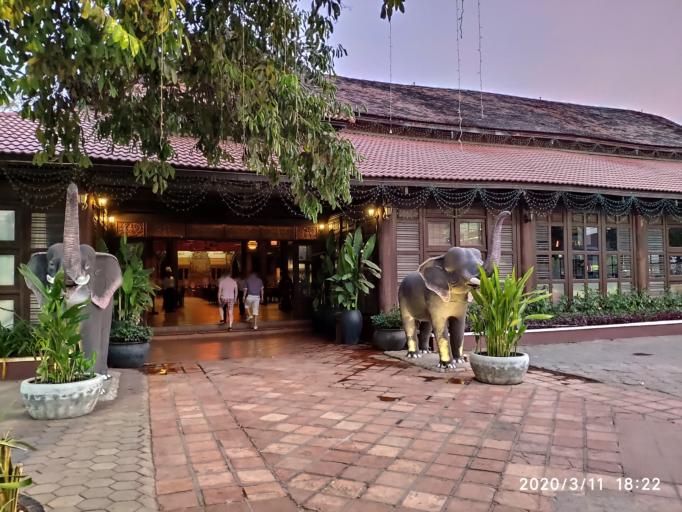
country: KH
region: Siem Reap
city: Siem Reap
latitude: 13.3622
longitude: 103.8561
